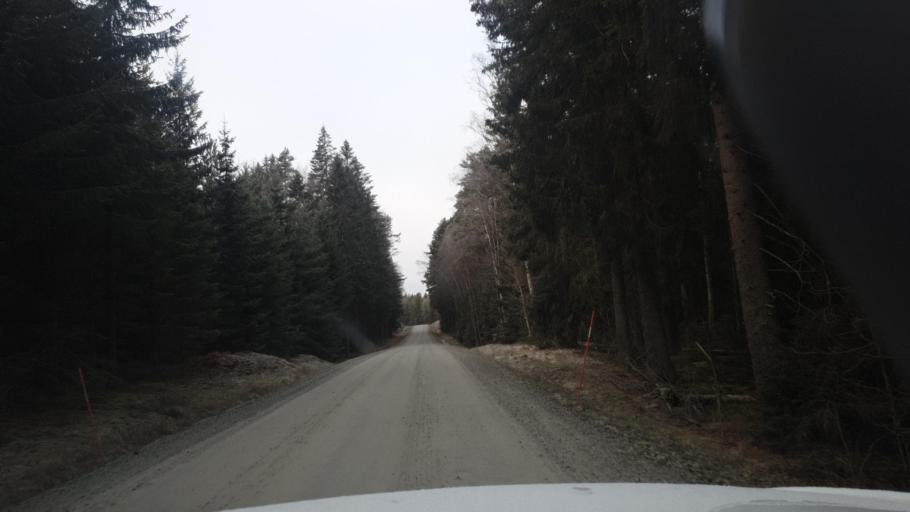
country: SE
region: Vaermland
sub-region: Karlstads Kommun
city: Valberg
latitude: 59.4505
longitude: 13.1042
